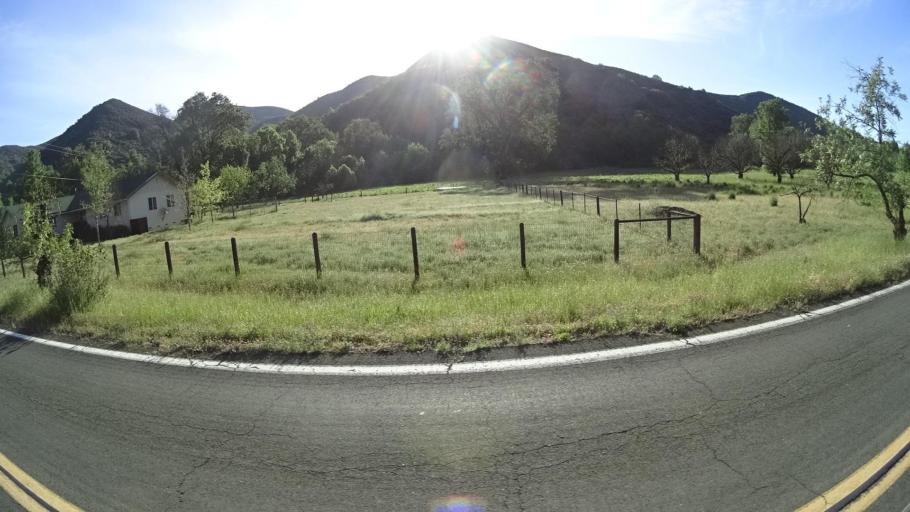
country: US
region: California
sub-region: Lake County
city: Upper Lake
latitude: 39.1337
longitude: -122.9982
